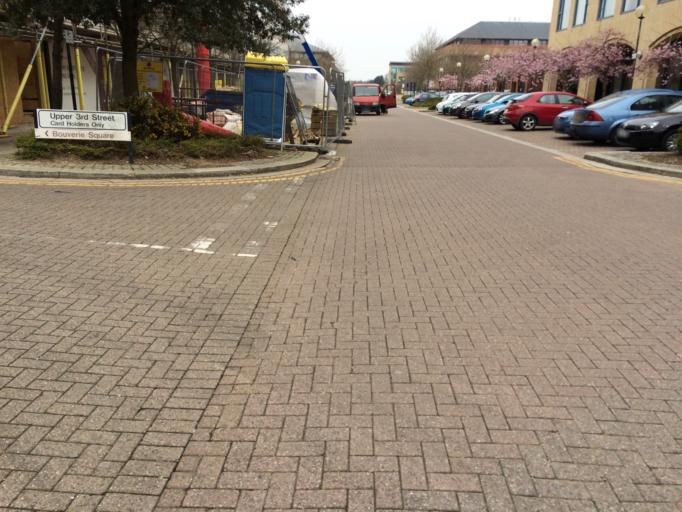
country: GB
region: England
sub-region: Milton Keynes
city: Milton Keynes
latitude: 52.0385
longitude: -0.7673
